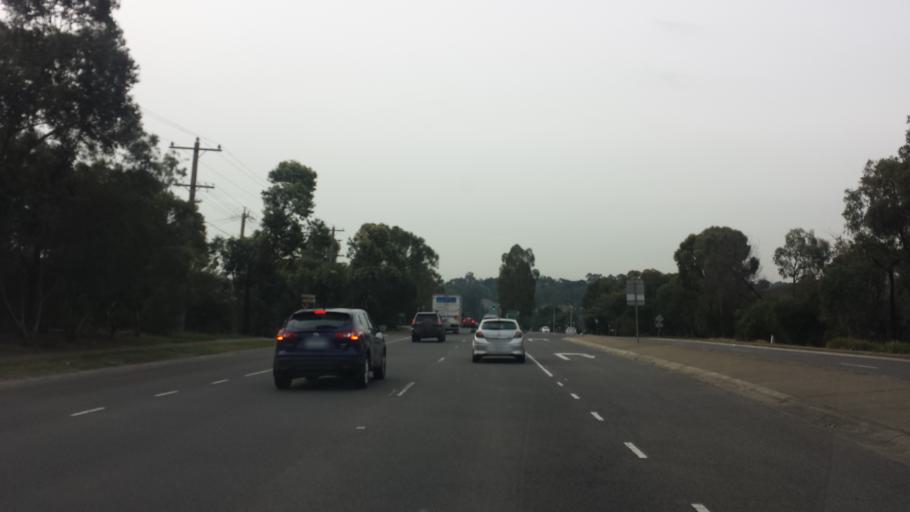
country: AU
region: Victoria
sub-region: Manningham
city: Templestowe Lower
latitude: -37.7721
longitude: 145.1281
